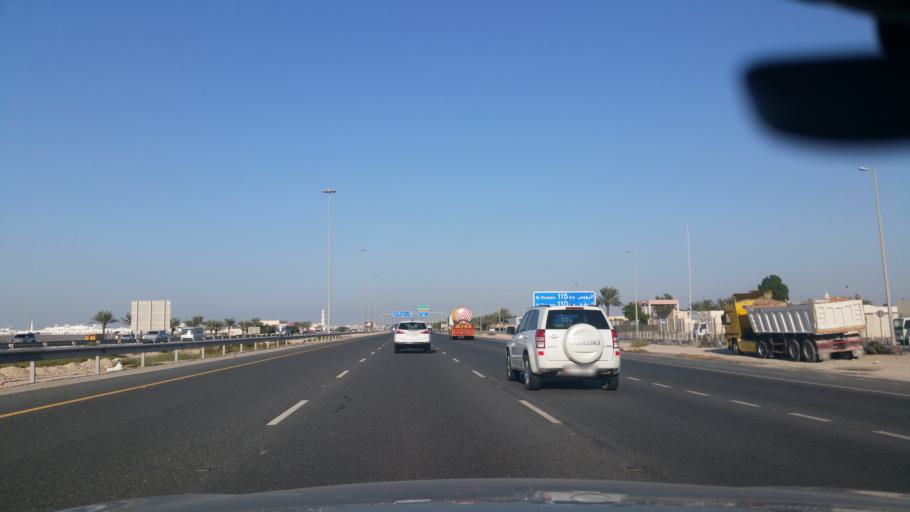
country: QA
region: Baladiyat ar Rayyan
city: Ar Rayyan
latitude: 25.2185
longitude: 51.4201
